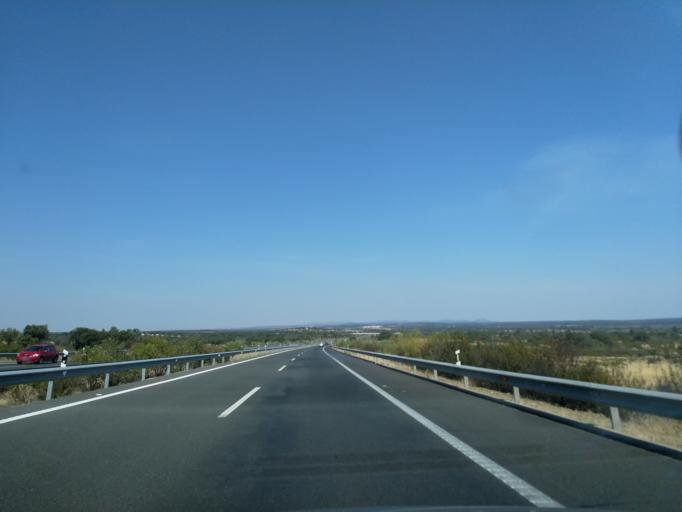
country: ES
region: Extremadura
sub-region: Provincia de Caceres
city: Alcuescar
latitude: 39.1800
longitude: -6.2738
